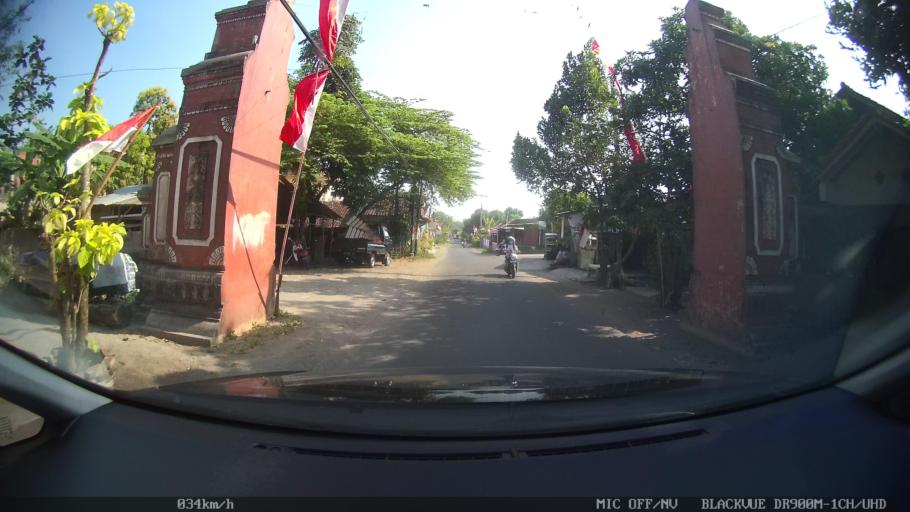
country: ID
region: Daerah Istimewa Yogyakarta
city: Kasihan
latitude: -7.8400
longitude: 110.3340
